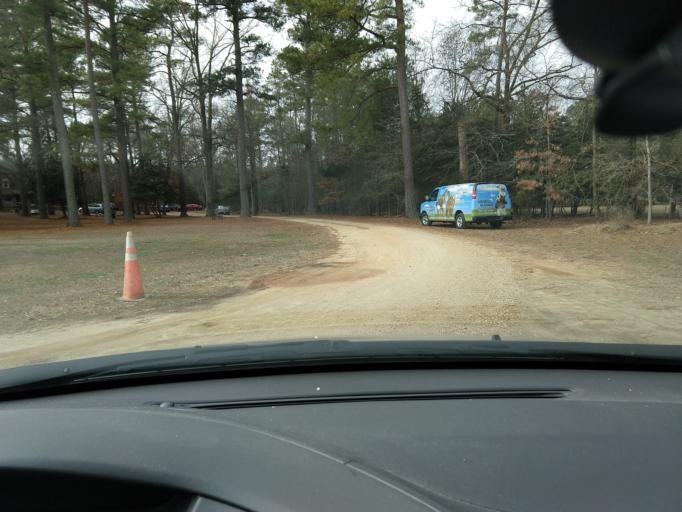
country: US
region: Virginia
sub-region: Chesterfield County
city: Bellwood
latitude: 37.4219
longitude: -77.3823
